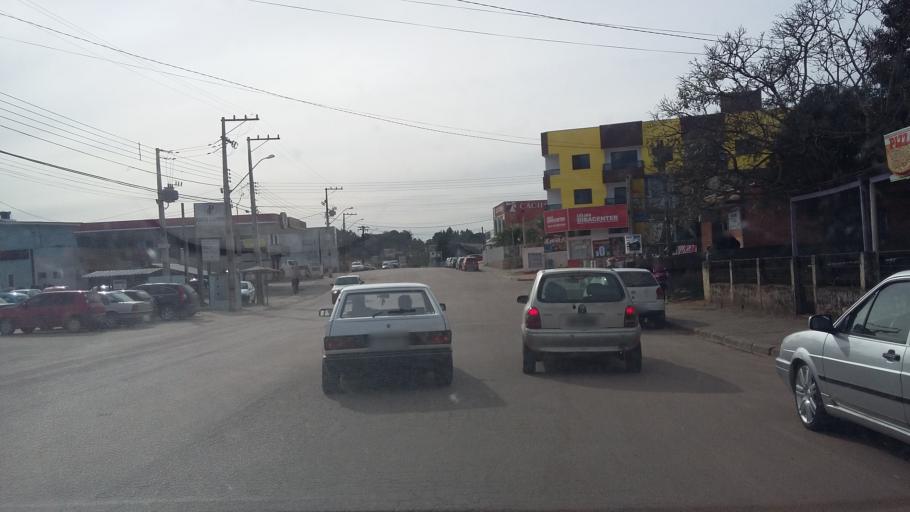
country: BR
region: Parana
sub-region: Lapa
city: Lapa
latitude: -25.8693
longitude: -49.5016
